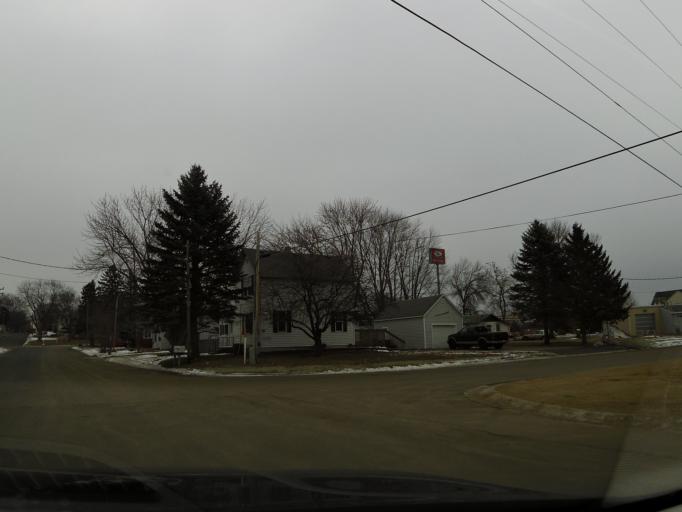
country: US
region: Minnesota
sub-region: Carver County
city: Cologne
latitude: 44.7676
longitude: -93.7832
